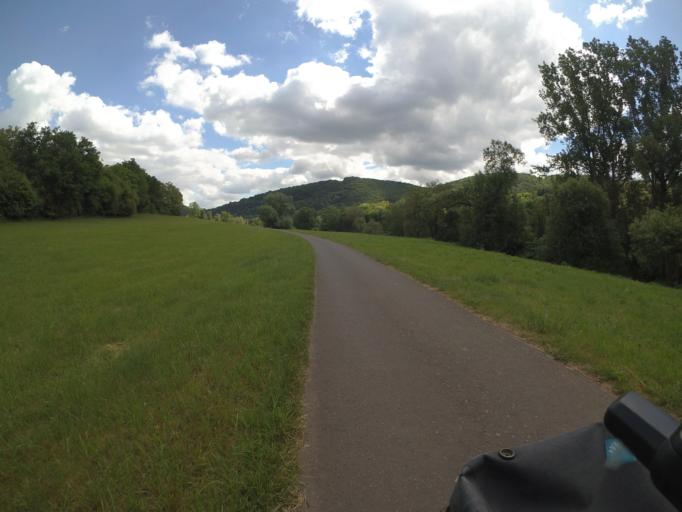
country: DE
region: Rheinland-Pfalz
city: Odernheim
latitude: 49.7742
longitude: 7.7081
